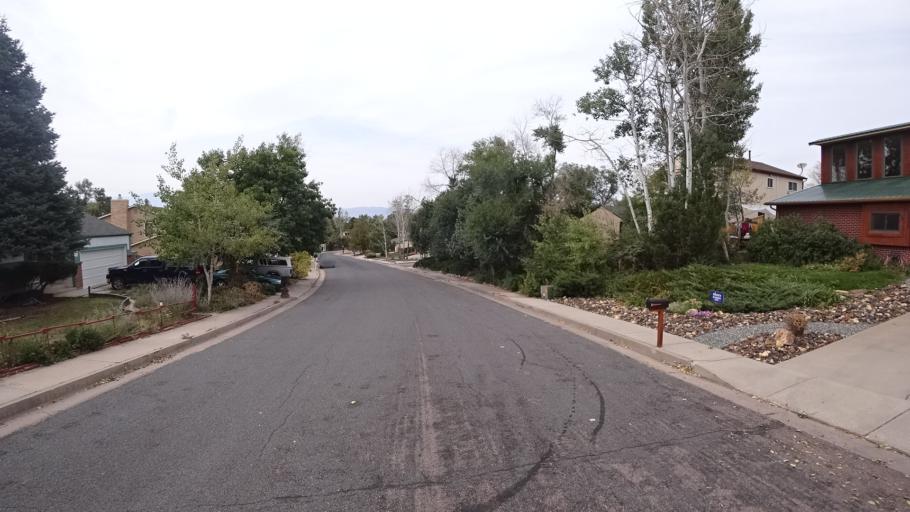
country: US
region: Colorado
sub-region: El Paso County
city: Cimarron Hills
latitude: 38.9031
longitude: -104.7226
